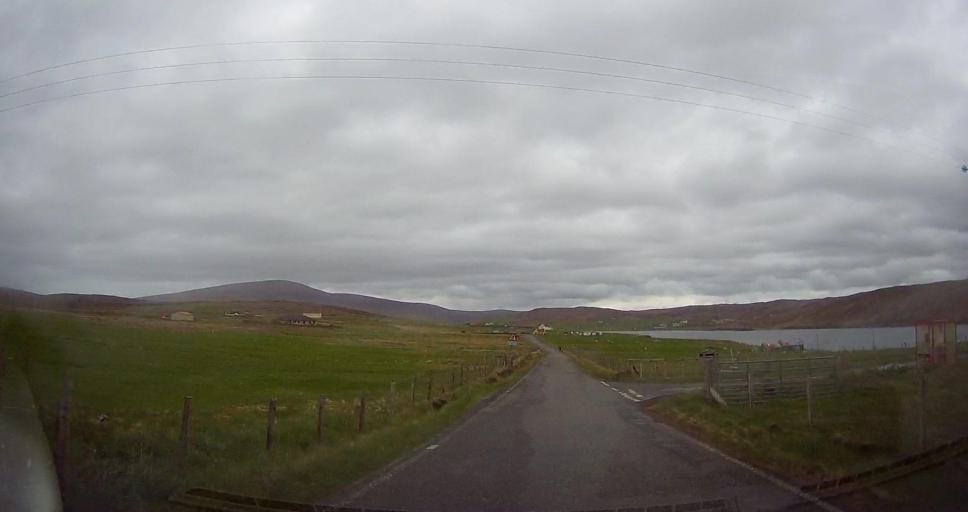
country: GB
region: Scotland
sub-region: Shetland Islands
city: Lerwick
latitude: 60.4786
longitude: -1.4815
